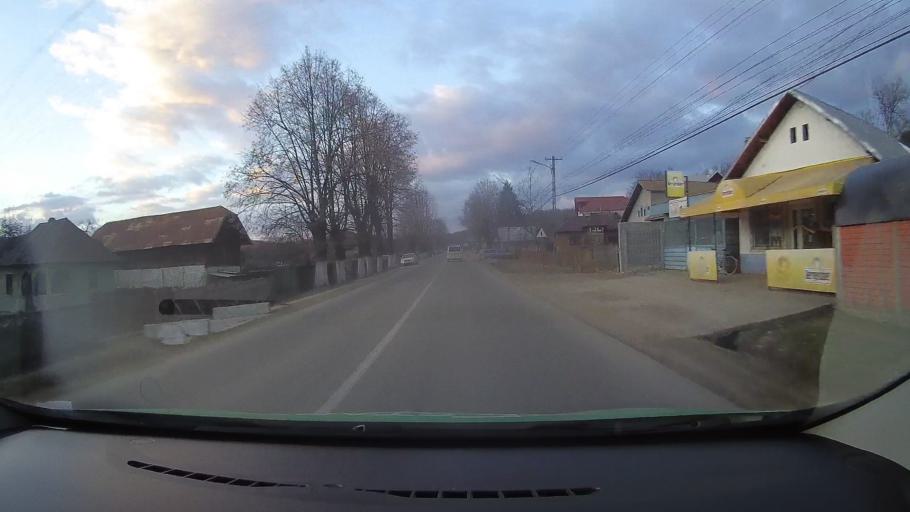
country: RO
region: Dambovita
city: Iedera de Jos
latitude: 45.0239
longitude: 25.6358
